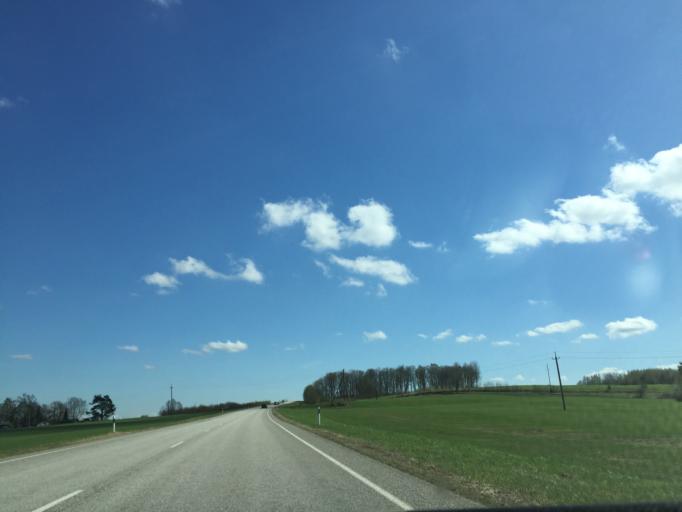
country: EE
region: Valgamaa
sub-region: Valga linn
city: Valga
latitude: 57.9080
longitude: 26.0429
